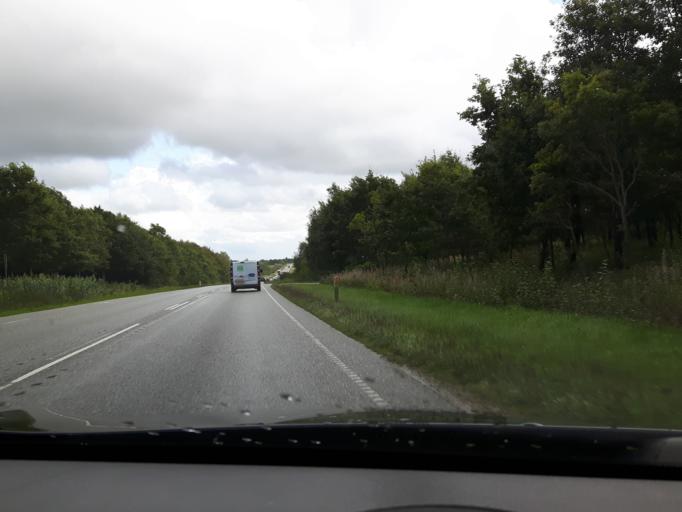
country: DK
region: Central Jutland
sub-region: Herning Kommune
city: Avlum
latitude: 56.2847
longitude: 8.7455
